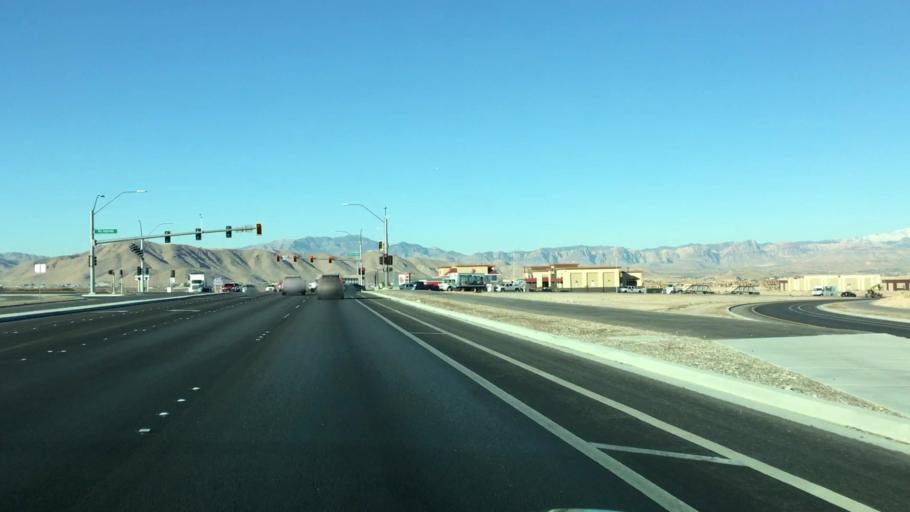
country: US
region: Nevada
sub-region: Clark County
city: Whitney
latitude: 35.9602
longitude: -115.1375
